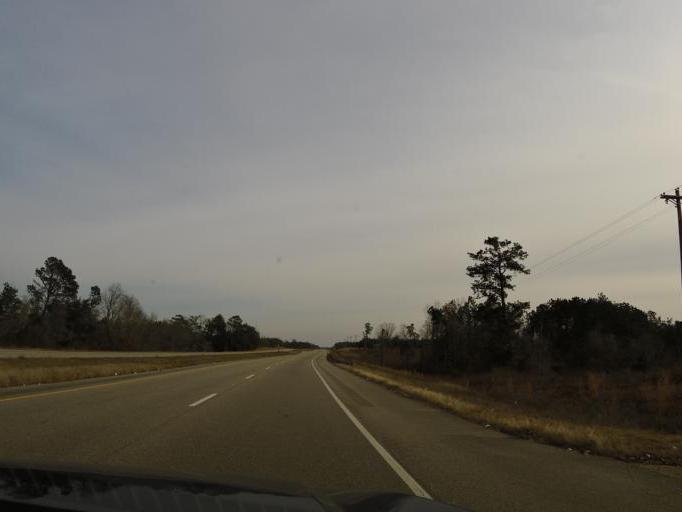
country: US
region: Alabama
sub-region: Houston County
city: Ashford
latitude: 31.1332
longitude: -85.0920
